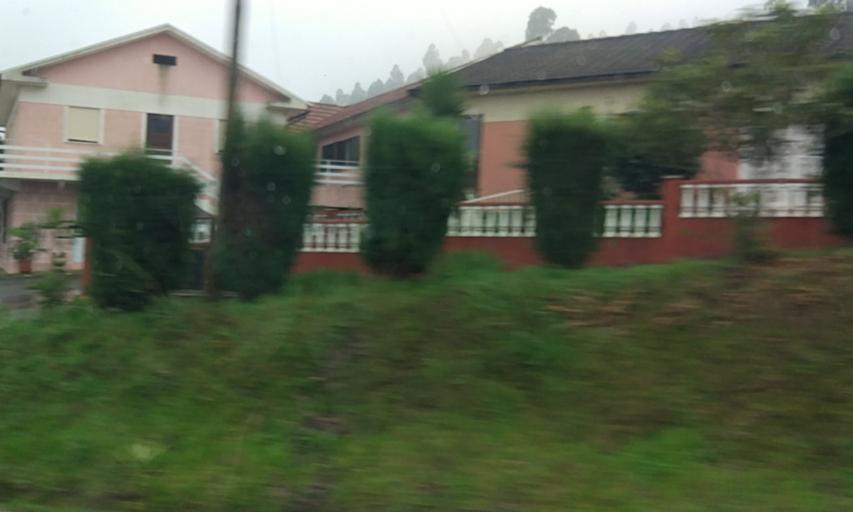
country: PT
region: Viseu
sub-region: Mortagua
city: Mortagua
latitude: 40.3883
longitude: -8.2986
